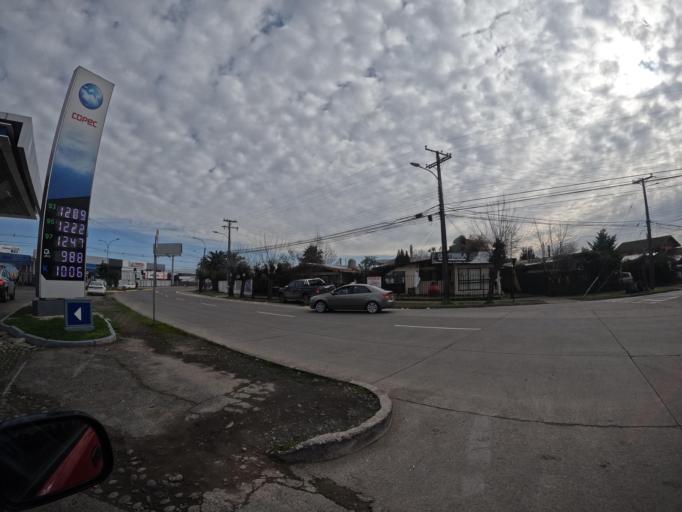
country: CL
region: Maule
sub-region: Provincia de Linares
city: Linares
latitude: -35.8443
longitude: -71.6045
